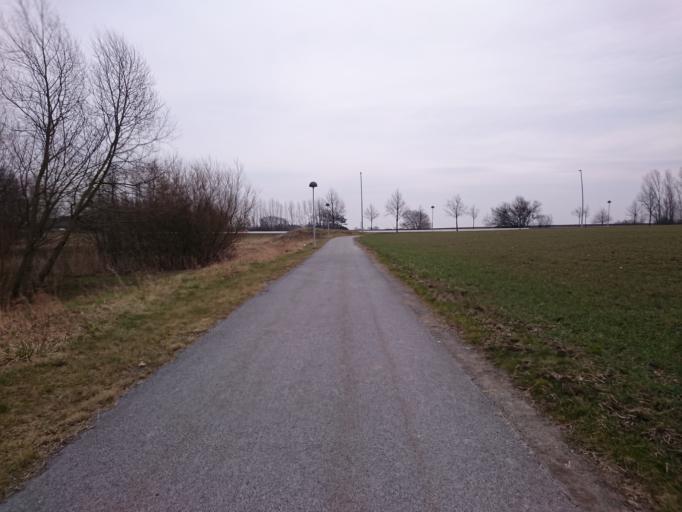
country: SE
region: Skane
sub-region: Lunds Kommun
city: Lund
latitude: 55.6817
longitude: 13.1834
